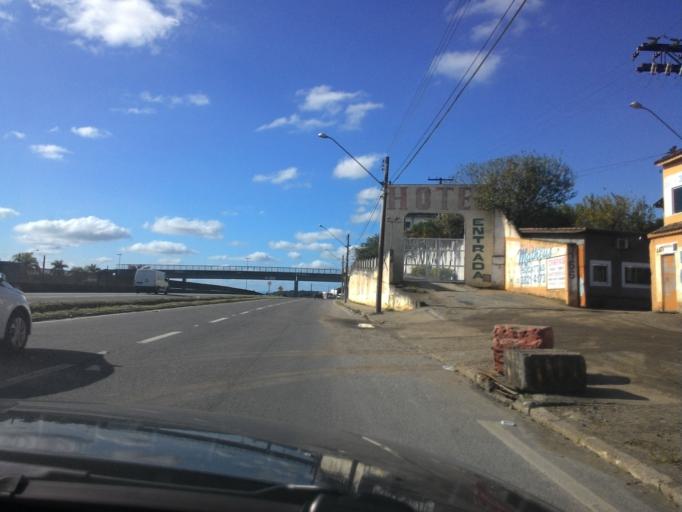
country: BR
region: Sao Paulo
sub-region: Registro
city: Registro
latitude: -24.4954
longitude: -47.8394
